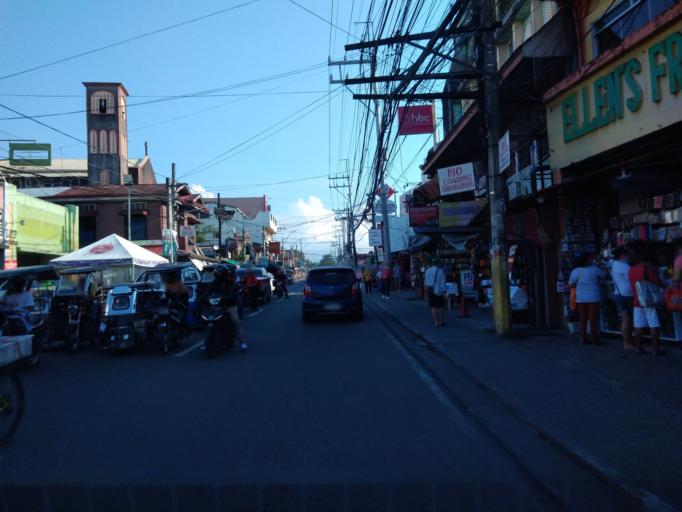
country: PH
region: Calabarzon
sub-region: Province of Laguna
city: Los Banos
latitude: 14.1779
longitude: 121.2423
